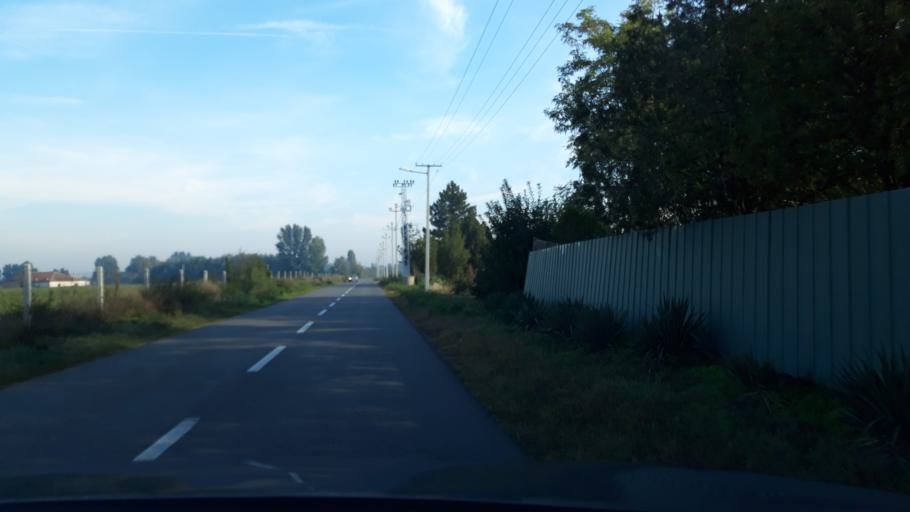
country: HU
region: Csongrad
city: Asotthalom
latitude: 46.1200
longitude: 19.8452
